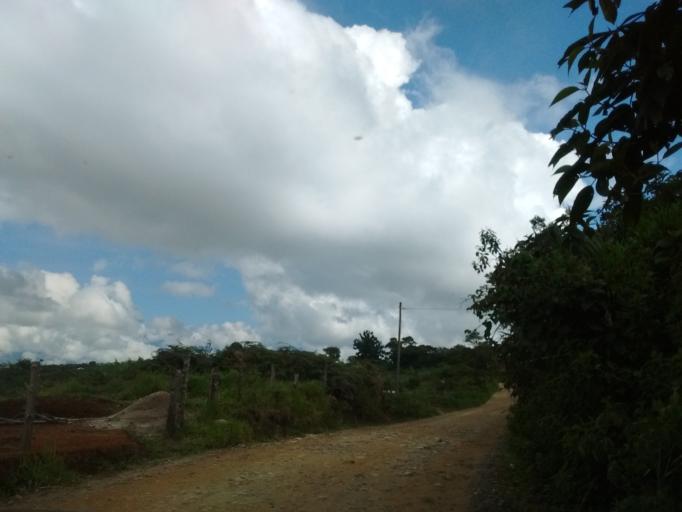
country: CO
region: Cauca
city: Cajibio
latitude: 2.6495
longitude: -76.6835
